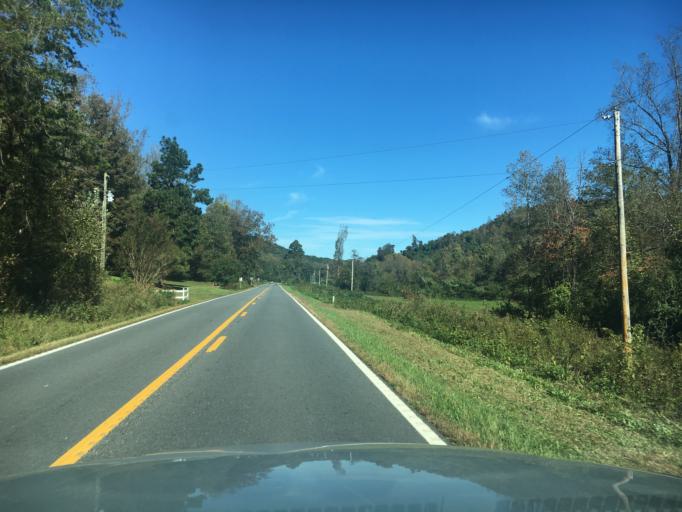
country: US
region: North Carolina
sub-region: Rutherford County
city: Spindale
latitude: 35.5373
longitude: -81.8563
